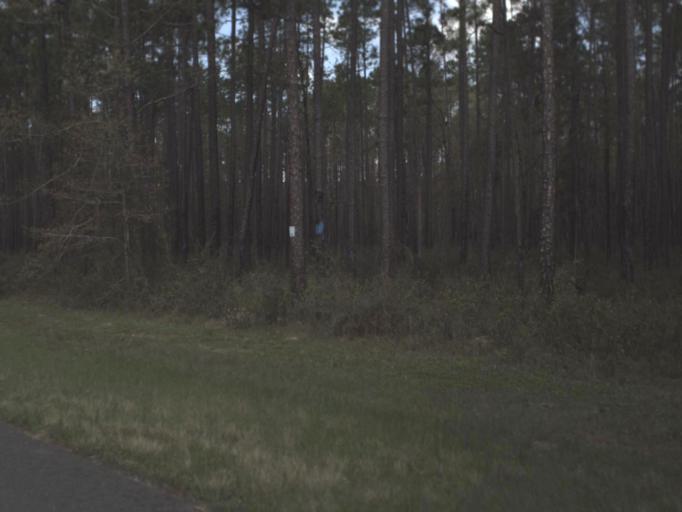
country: US
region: Florida
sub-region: Santa Rosa County
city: Point Baker
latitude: 30.8549
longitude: -86.8444
